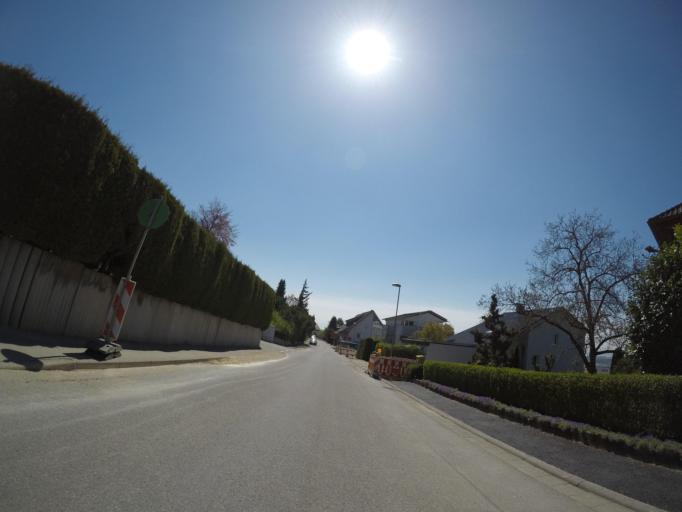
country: DE
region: Baden-Wuerttemberg
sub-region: Tuebingen Region
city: Markdorf
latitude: 47.7331
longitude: 9.3878
